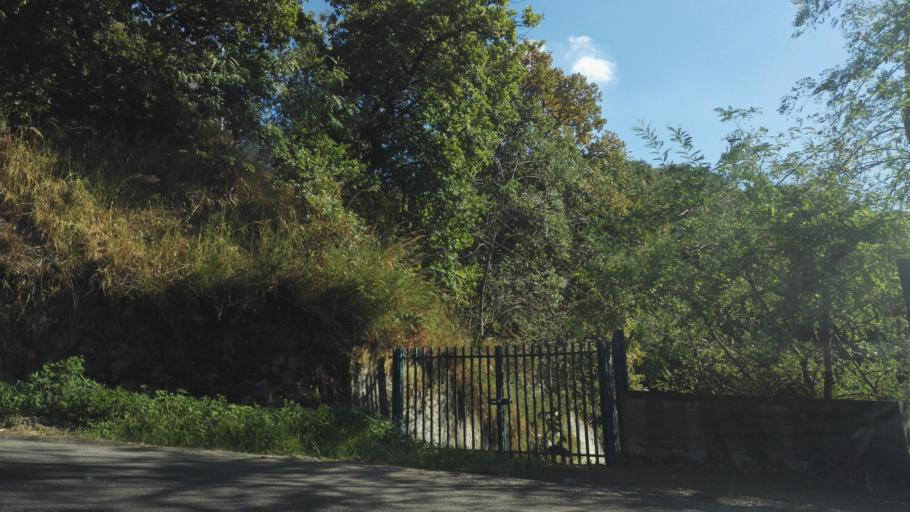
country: IT
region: Calabria
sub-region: Provincia di Vibo-Valentia
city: Sorianello
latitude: 38.5937
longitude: 16.2296
